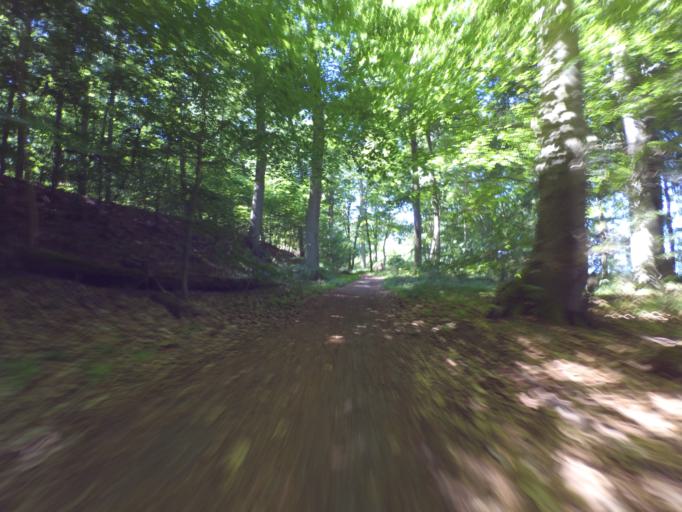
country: DE
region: Mecklenburg-Vorpommern
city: Malchow
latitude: 53.4751
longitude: 12.3536
